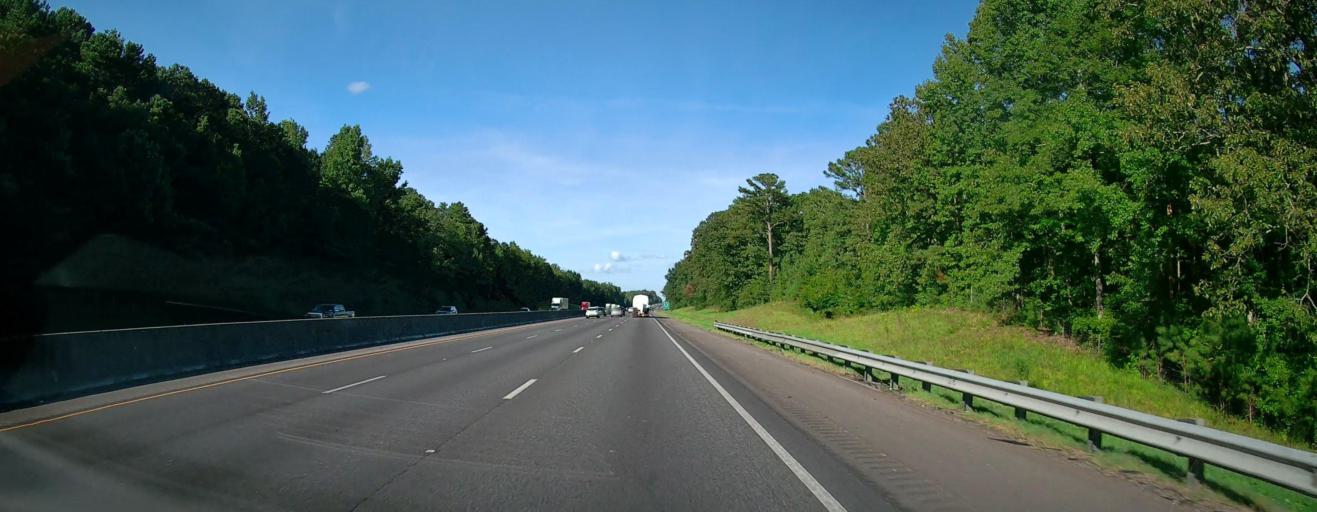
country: US
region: Alabama
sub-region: Bibb County
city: North Bibb
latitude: 33.2271
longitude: -87.1730
